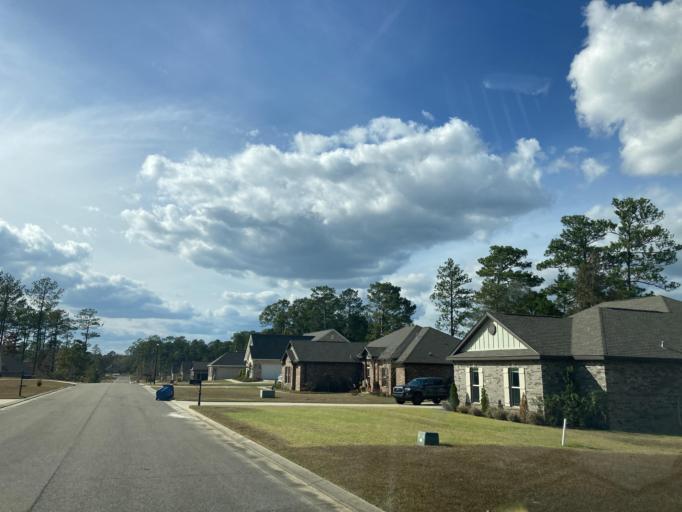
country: US
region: Mississippi
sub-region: Lamar County
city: Arnold Line
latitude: 31.3461
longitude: -89.3679
